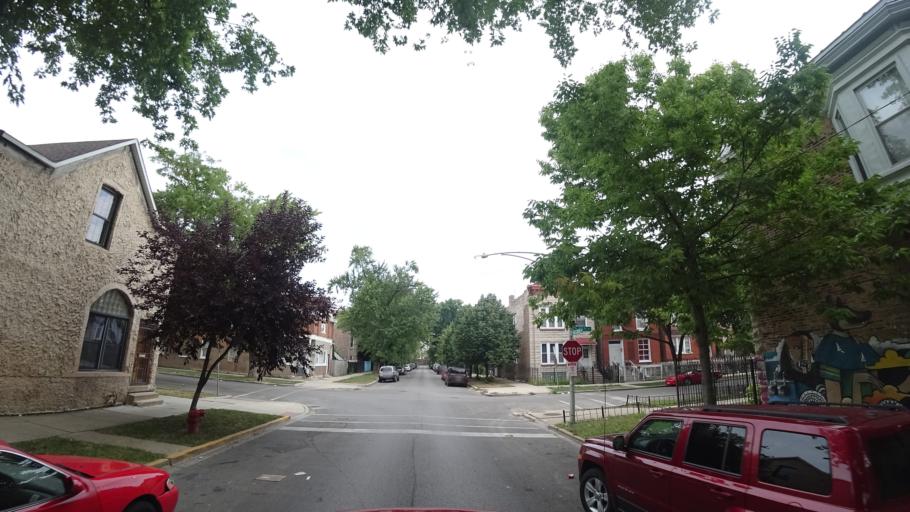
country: US
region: Illinois
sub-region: Cook County
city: Cicero
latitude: 41.8496
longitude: -87.7125
